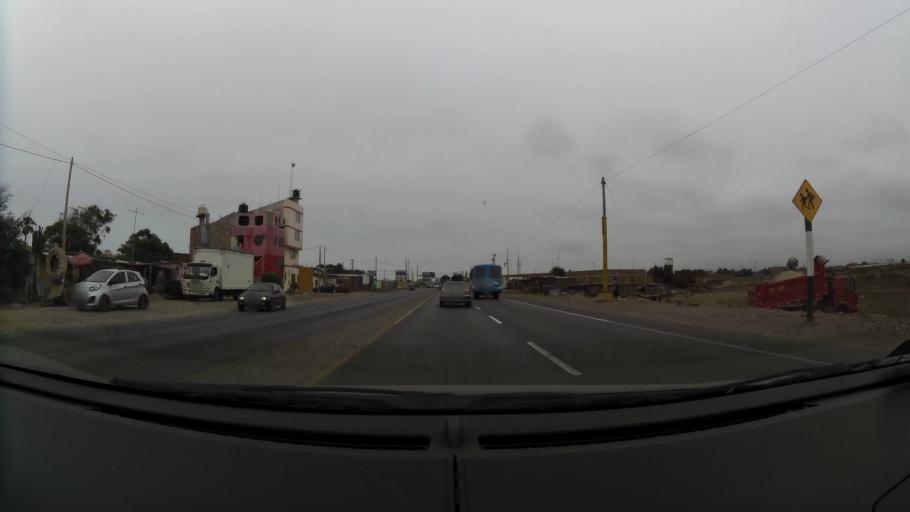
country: PE
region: La Libertad
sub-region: Provincia de Trujillo
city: Moche
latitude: -8.1689
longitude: -79.0049
